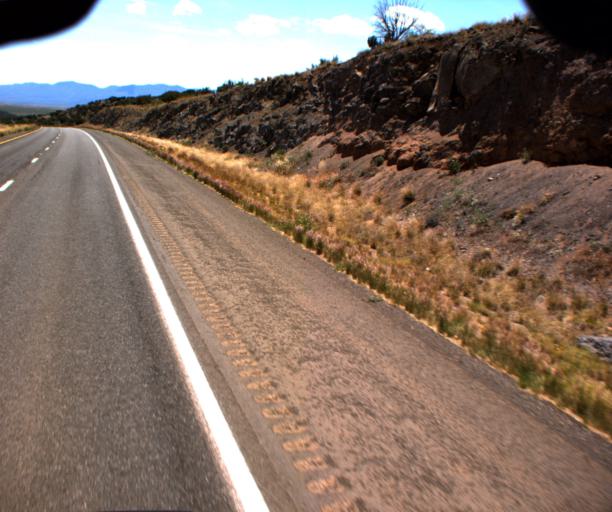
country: US
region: Arizona
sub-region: Yavapai County
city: Cornville
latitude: 34.8051
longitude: -111.9114
